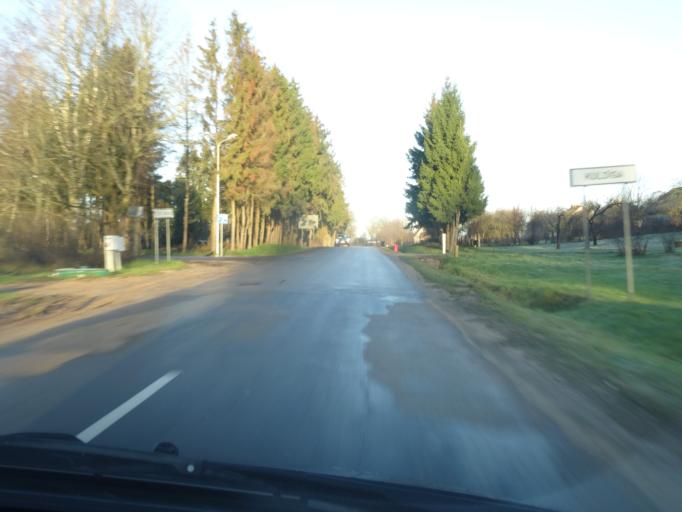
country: LV
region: Kuldigas Rajons
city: Kuldiga
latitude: 56.9696
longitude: 21.9992
